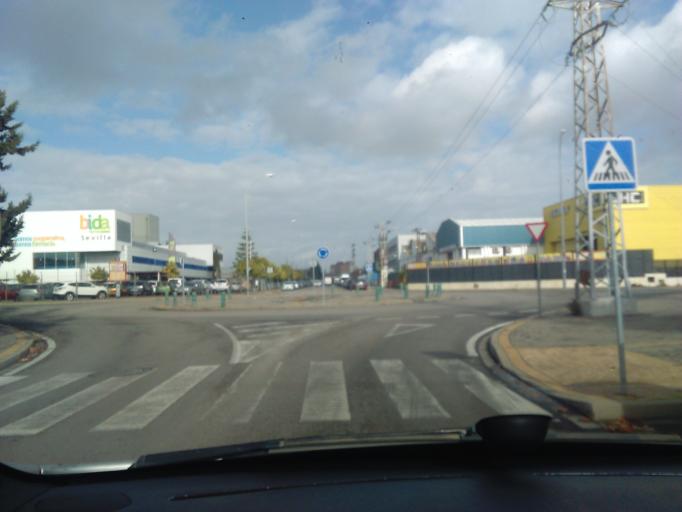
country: ES
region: Andalusia
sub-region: Provincia de Sevilla
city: Sevilla
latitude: 37.3769
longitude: -5.9263
